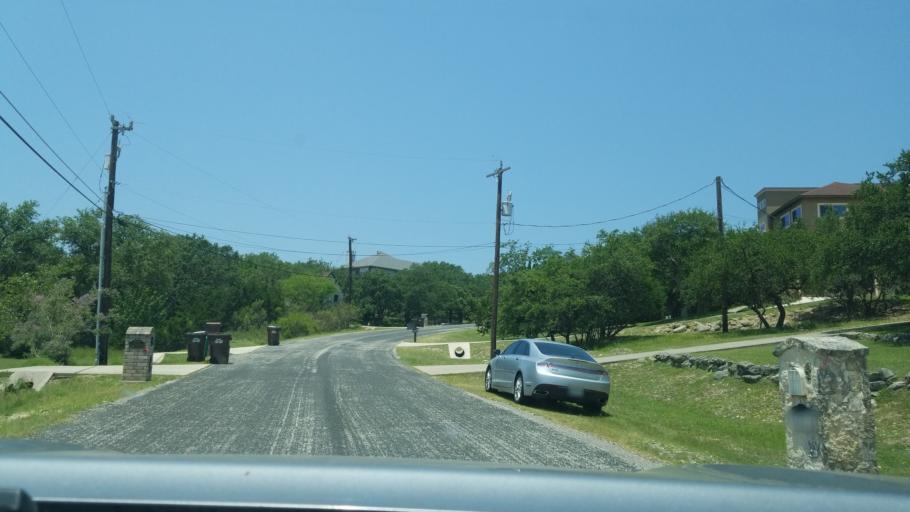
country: US
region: Texas
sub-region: Bexar County
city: Timberwood Park
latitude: 29.6865
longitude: -98.5142
